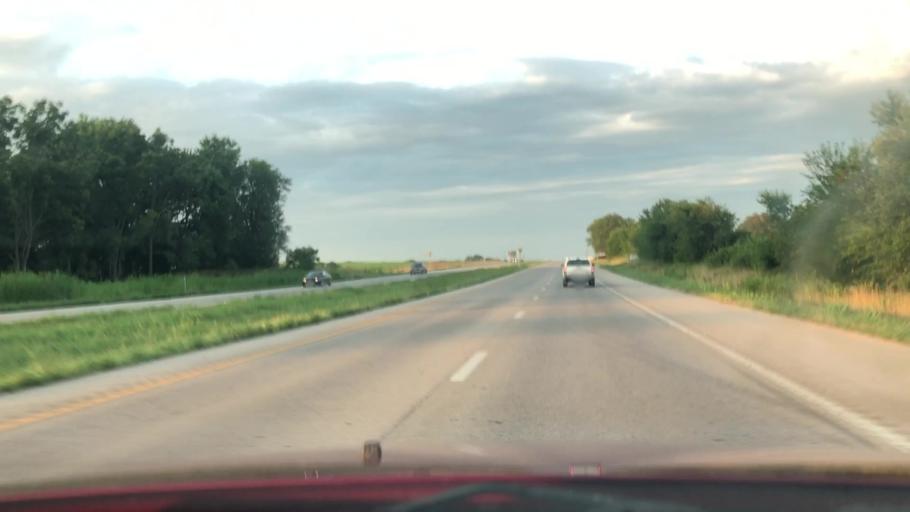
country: US
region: Missouri
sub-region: Greene County
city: Battlefield
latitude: 37.1497
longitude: -93.4213
